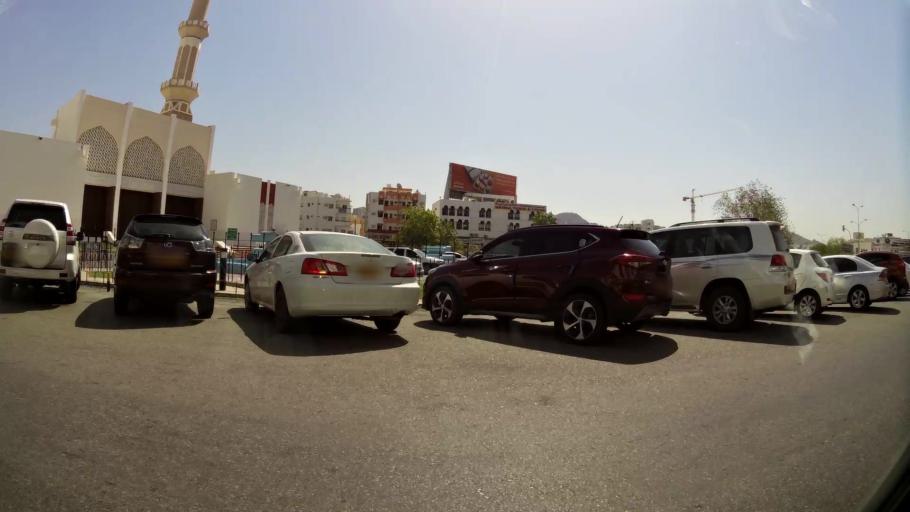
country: OM
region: Muhafazat Masqat
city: Muscat
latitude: 23.5949
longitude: 58.5437
